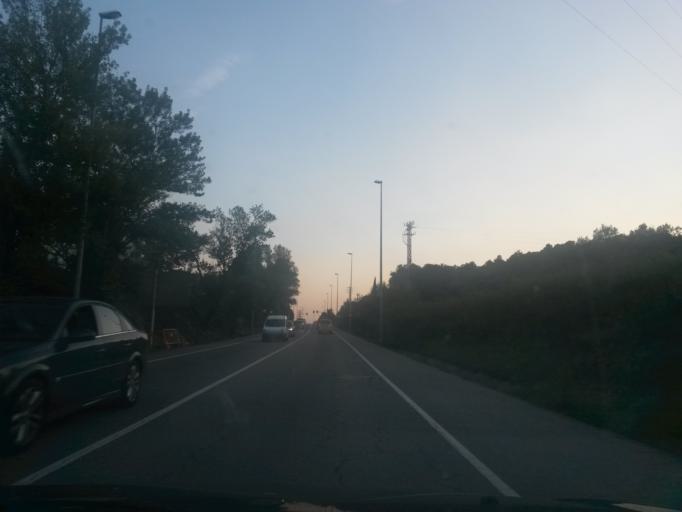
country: ES
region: Catalonia
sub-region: Provincia de Girona
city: Girona
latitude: 41.9992
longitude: 2.8172
